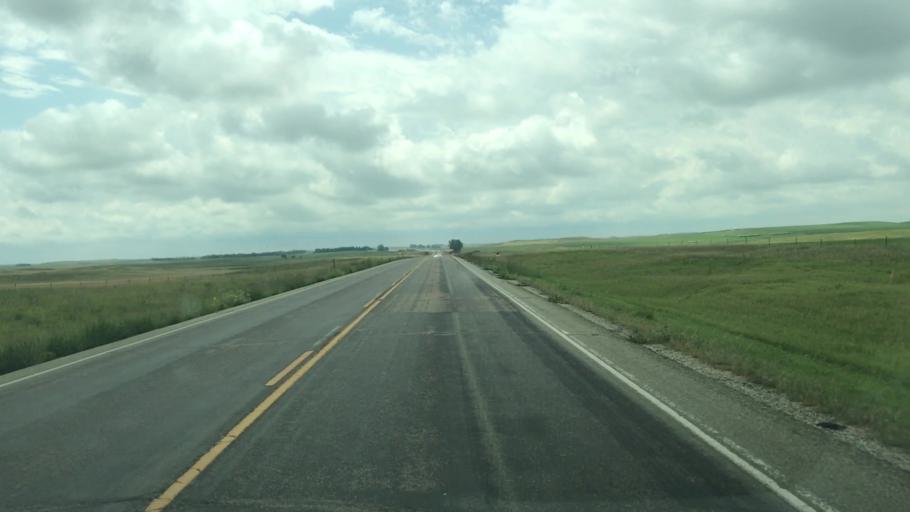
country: US
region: Nebraska
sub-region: Cherry County
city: Valentine
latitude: 43.0588
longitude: -100.5950
